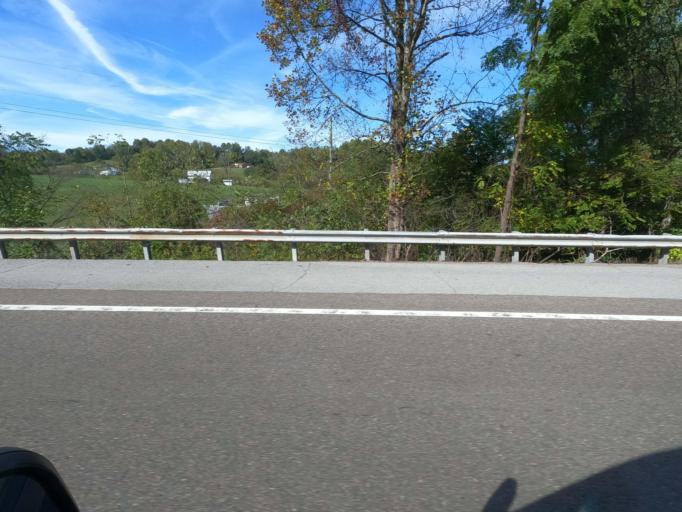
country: US
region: Tennessee
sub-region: Sullivan County
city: Walnut Hill
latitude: 36.5913
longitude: -82.2774
